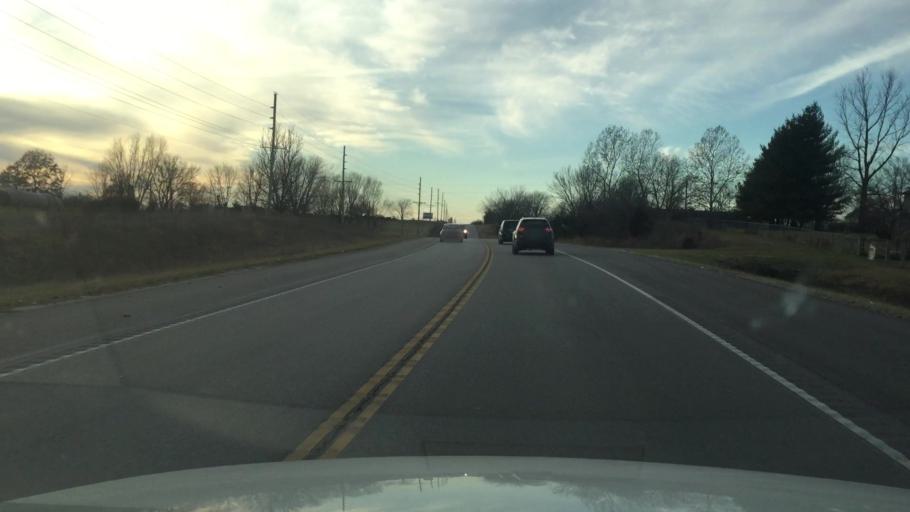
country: US
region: Missouri
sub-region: Miller County
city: Eldon
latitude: 38.3738
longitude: -92.6246
